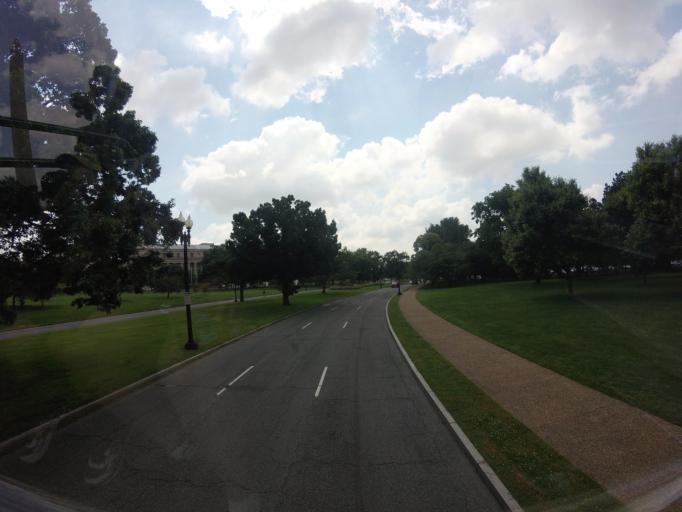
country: US
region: Washington, D.C.
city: Washington, D.C.
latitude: 38.8864
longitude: -77.0355
